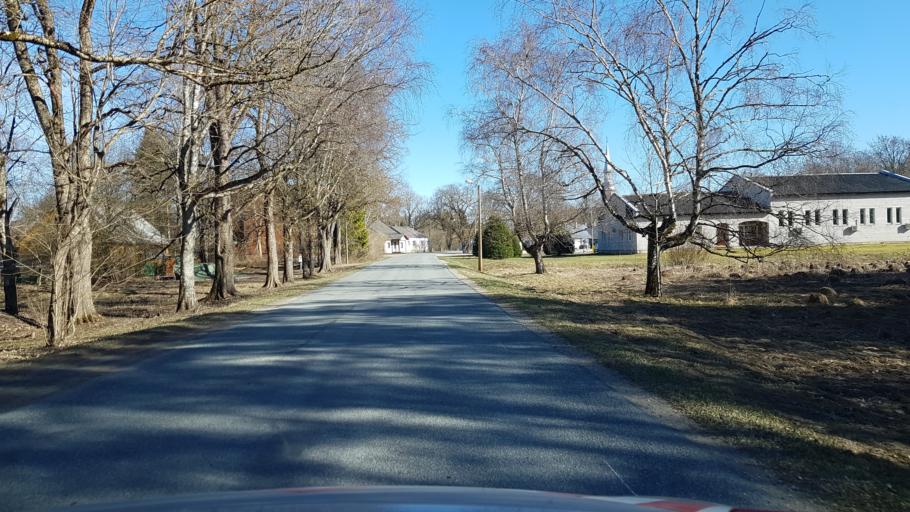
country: EE
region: Laeaene-Virumaa
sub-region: Rakke vald
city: Rakke
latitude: 59.0465
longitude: 26.3980
